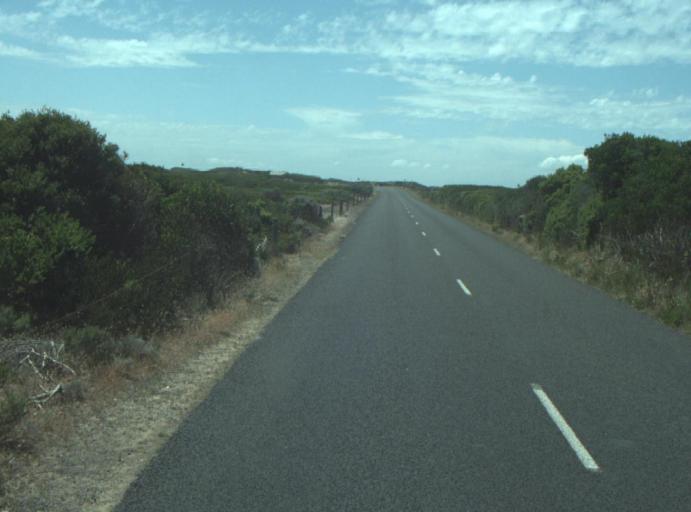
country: AU
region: Victoria
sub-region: Greater Geelong
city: Leopold
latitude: -38.2875
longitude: 144.4766
